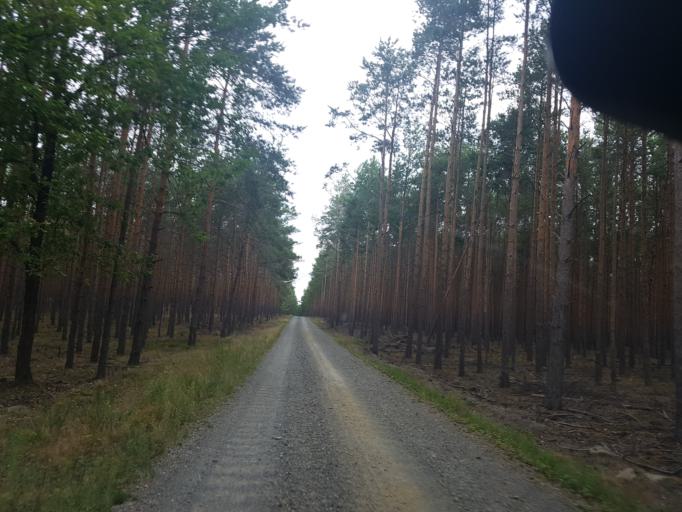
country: DE
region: Brandenburg
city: Sallgast
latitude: 51.6246
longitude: 13.8043
